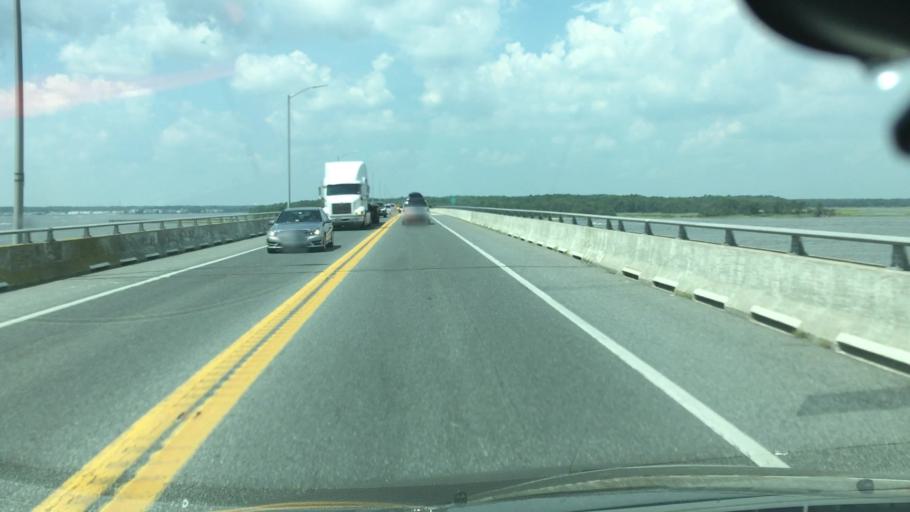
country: US
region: Maryland
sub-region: Worcester County
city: Ocean City
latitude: 38.3885
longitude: -75.0902
